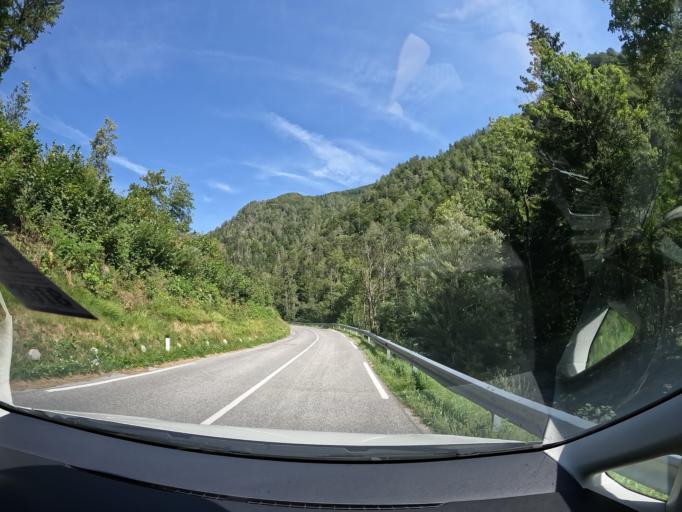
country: SI
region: Zirovnica
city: Zirovnica
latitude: 46.4398
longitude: 14.1544
